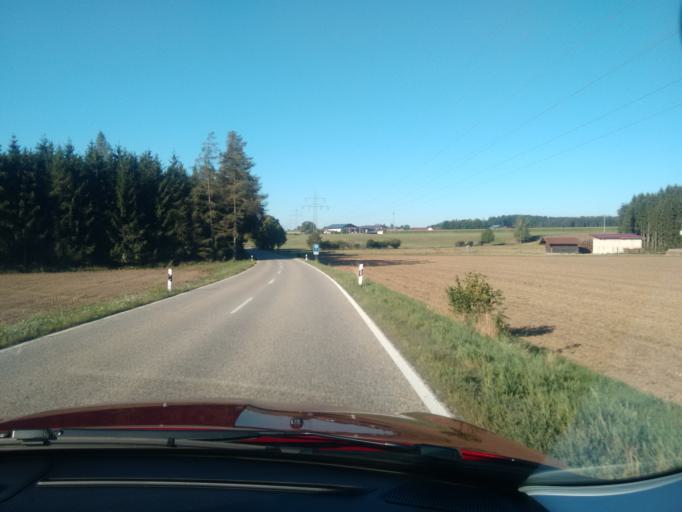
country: DE
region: Bavaria
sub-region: Upper Bavaria
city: Kirchweidach
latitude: 48.0708
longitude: 12.6171
